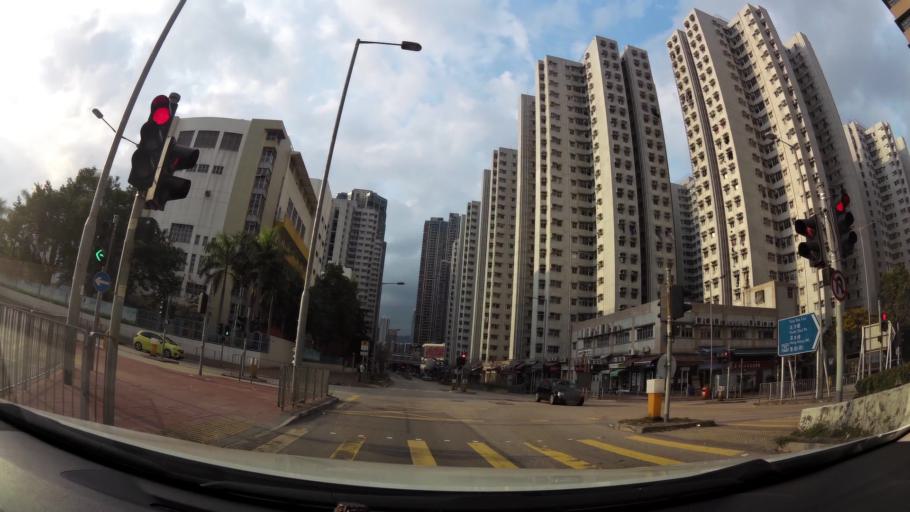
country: HK
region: Sham Shui Po
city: Sham Shui Po
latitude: 22.3129
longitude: 114.1645
